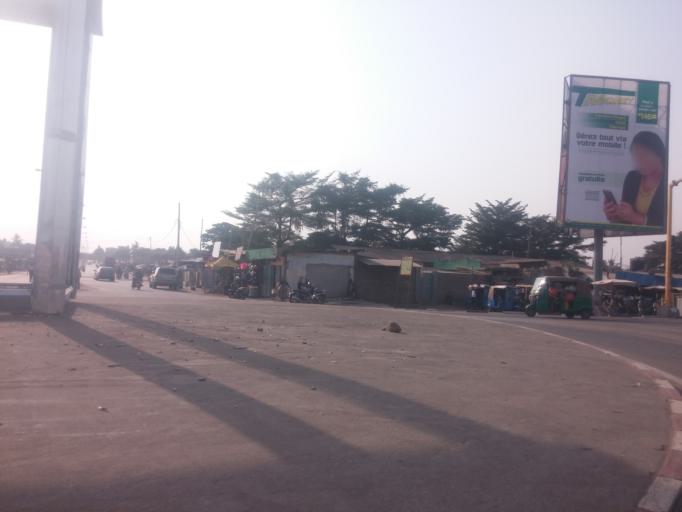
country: TG
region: Maritime
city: Lome
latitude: 6.1705
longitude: 1.2825
